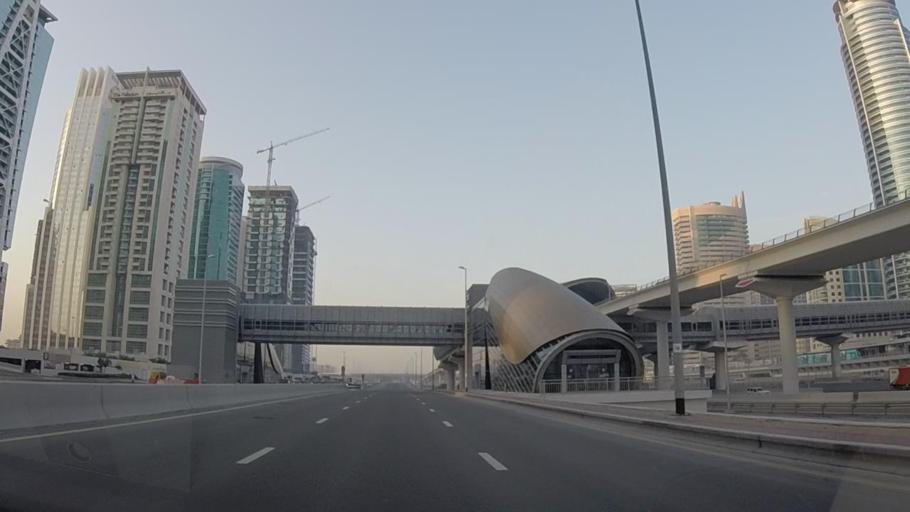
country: AE
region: Dubai
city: Dubai
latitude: 25.0719
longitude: 55.1401
